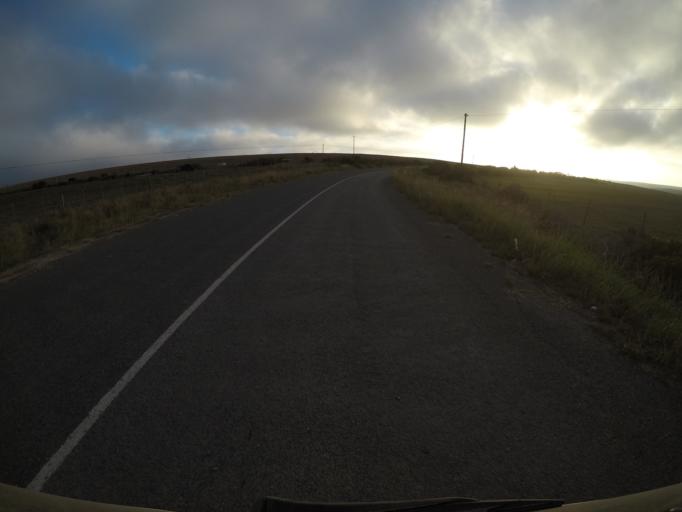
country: ZA
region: Western Cape
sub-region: Eden District Municipality
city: Mossel Bay
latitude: -34.1096
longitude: 22.0731
